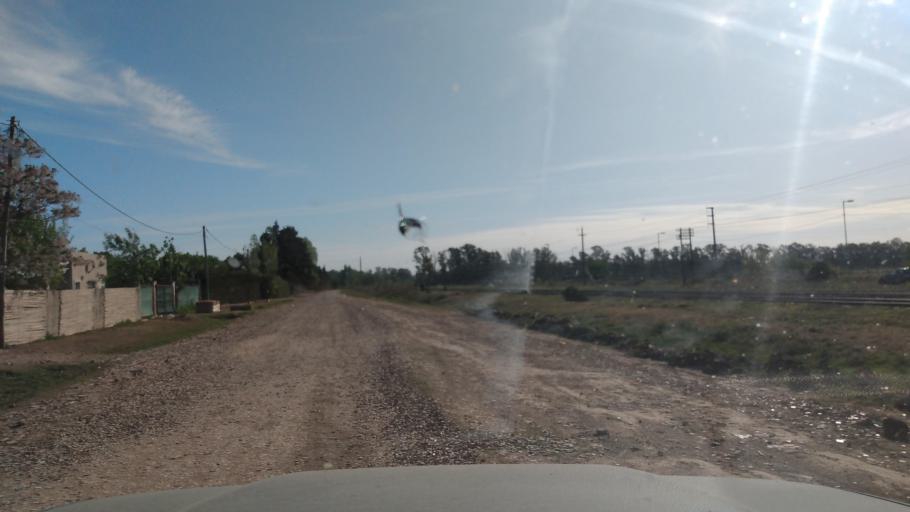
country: AR
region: Buenos Aires
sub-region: Partido de Lujan
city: Lujan
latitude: -34.5908
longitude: -59.1434
